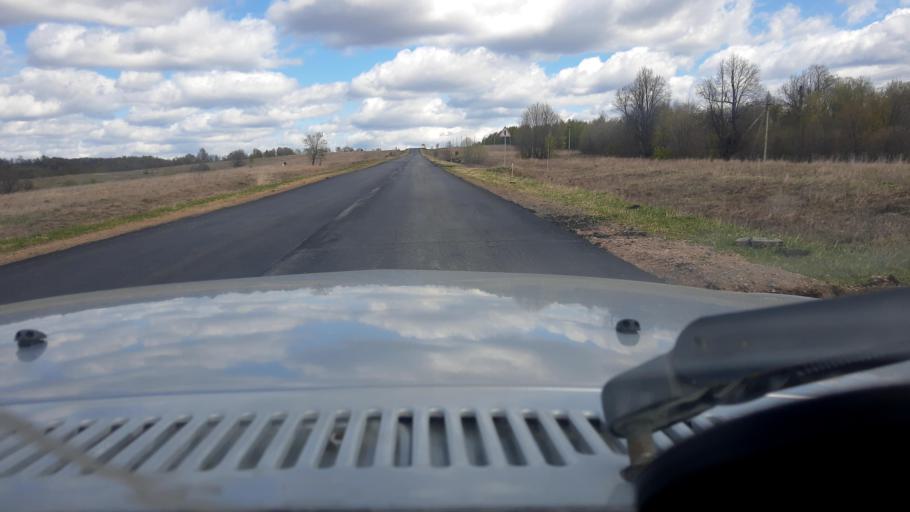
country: RU
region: Bashkortostan
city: Pavlovka
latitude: 55.3562
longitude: 56.4055
